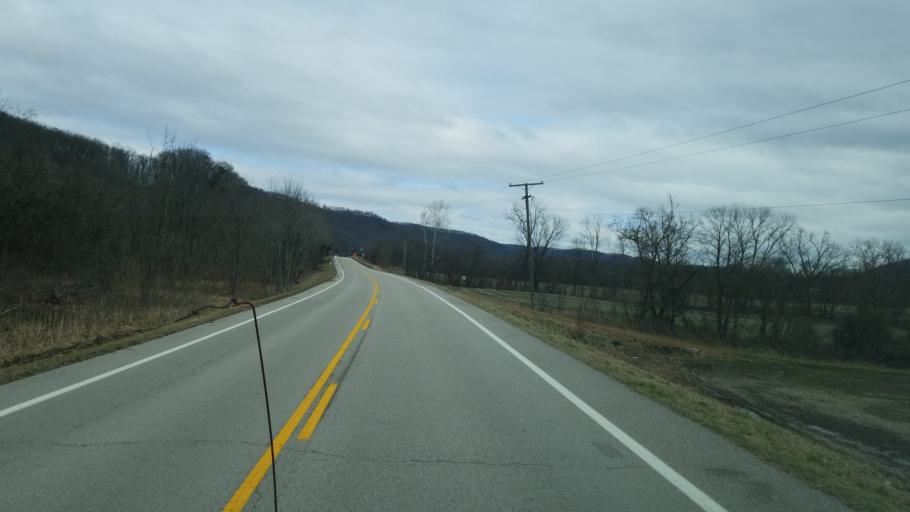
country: US
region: Kentucky
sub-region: Lewis County
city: Vanceburg
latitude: 38.6684
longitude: -83.3978
